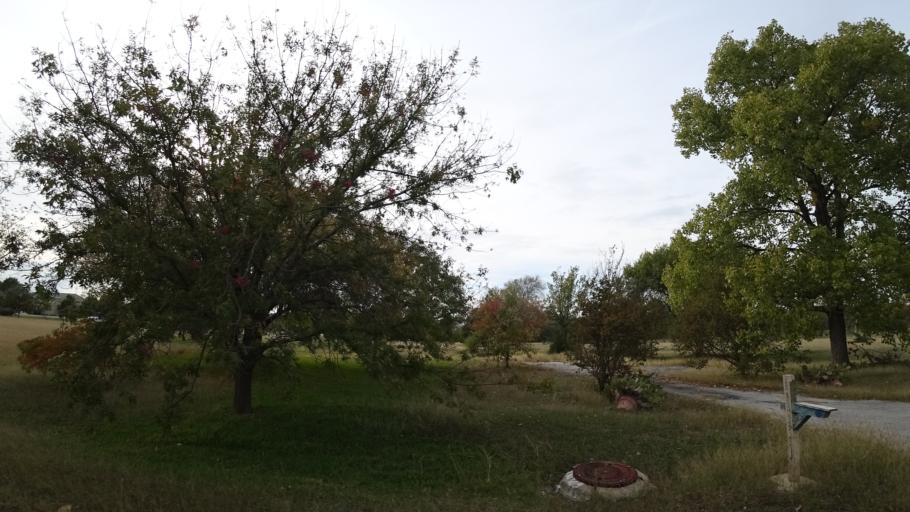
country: US
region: Texas
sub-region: Williamson County
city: Round Rock
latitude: 30.4969
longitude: -97.6583
